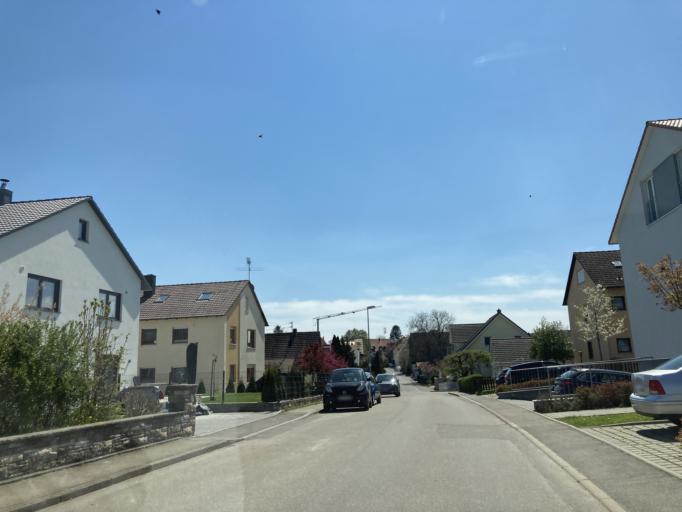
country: DE
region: Baden-Wuerttemberg
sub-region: Tuebingen Region
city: Rottenburg
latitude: 48.4848
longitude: 8.8859
